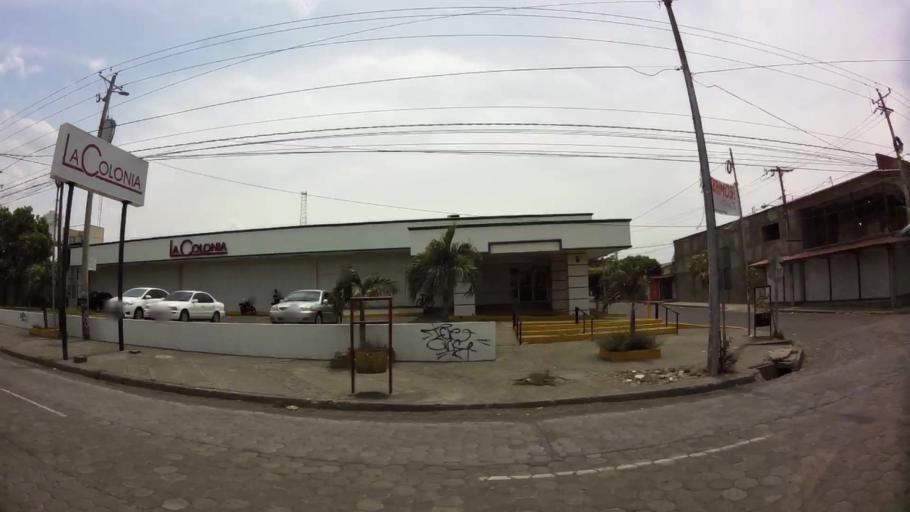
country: NI
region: Managua
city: Ciudad Sandino
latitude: 12.1500
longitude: -86.3047
